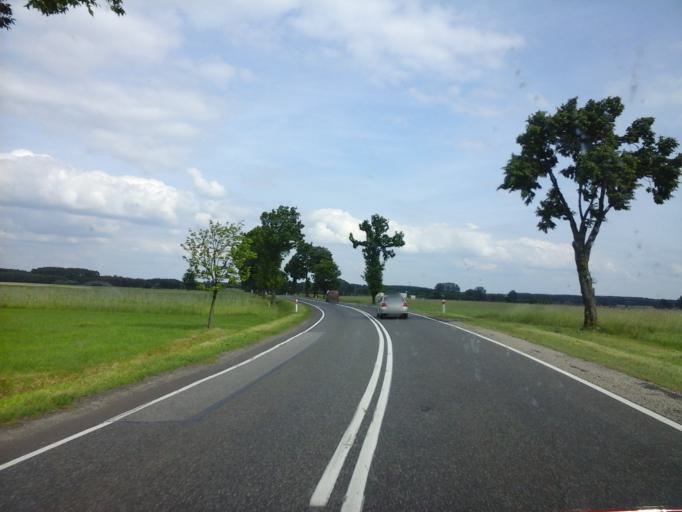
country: PL
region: Lodz Voivodeship
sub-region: Powiat opoczynski
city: Mniszkow
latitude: 51.3190
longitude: 20.0539
